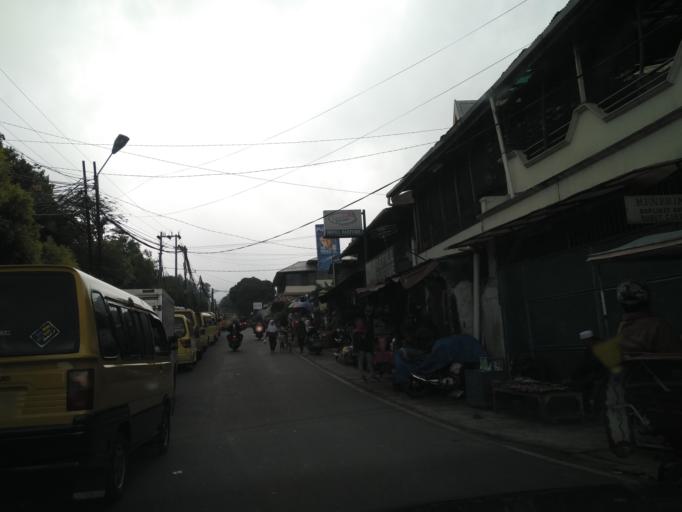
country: ID
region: West Java
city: Sukabumi
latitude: -6.7313
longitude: 107.0411
